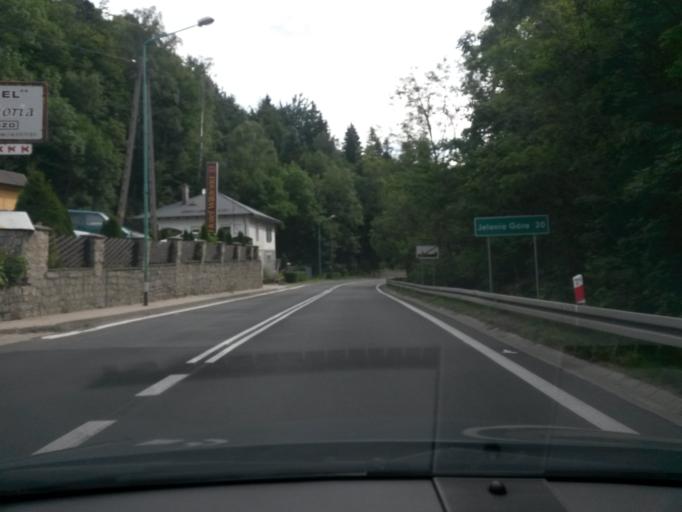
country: PL
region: Lower Silesian Voivodeship
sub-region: Powiat jeleniogorski
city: Szklarska Poreba
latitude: 50.8278
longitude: 15.5276
